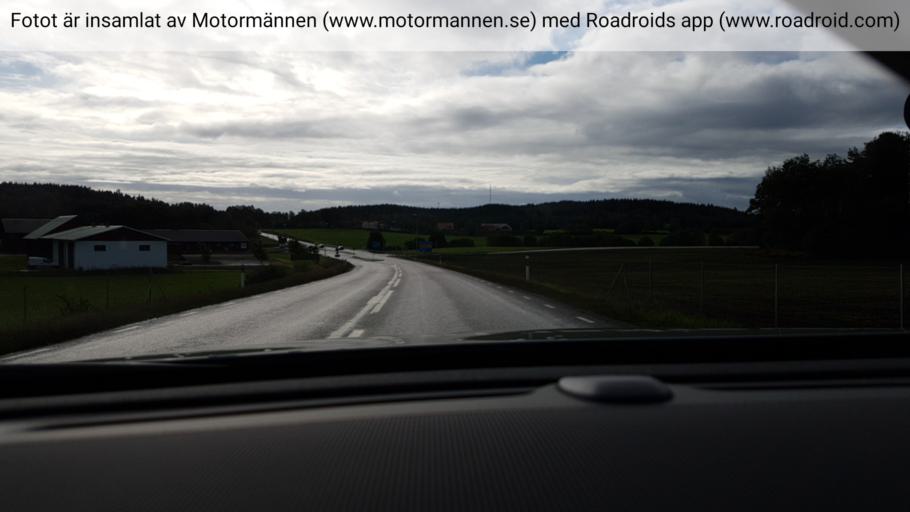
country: SE
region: Vaestra Goetaland
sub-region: Harryda Kommun
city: Ravlanda
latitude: 57.5565
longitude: 12.5195
